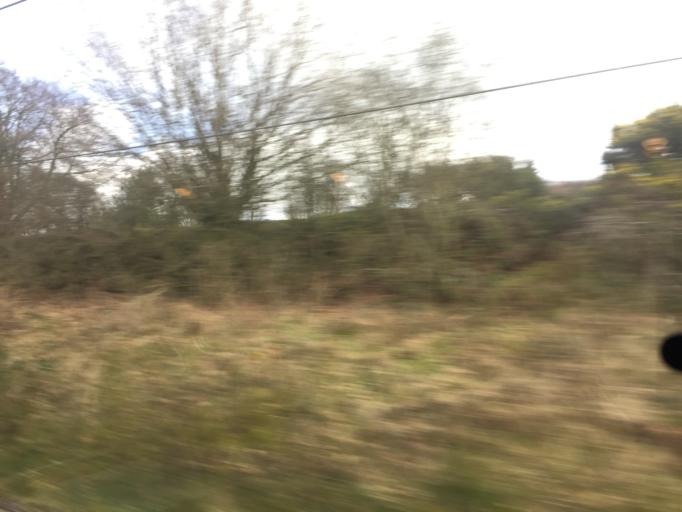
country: GB
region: Scotland
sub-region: Dumfries and Galloway
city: Lockerbie
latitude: 55.1731
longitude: -3.3939
